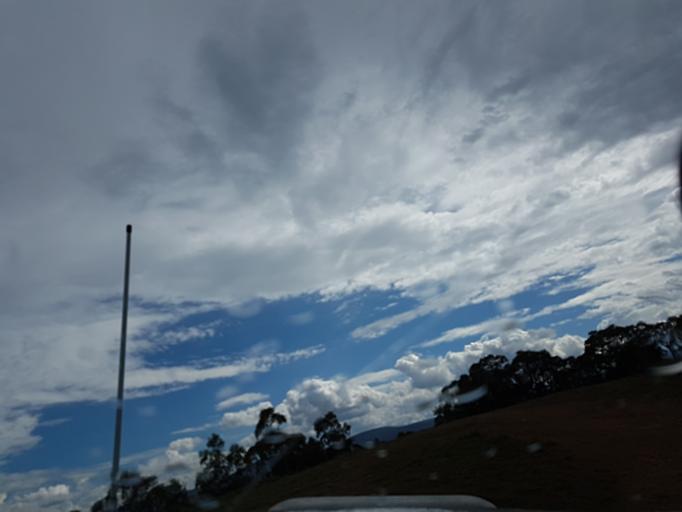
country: AU
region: New South Wales
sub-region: Snowy River
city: Jindabyne
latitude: -36.9107
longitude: 148.3367
